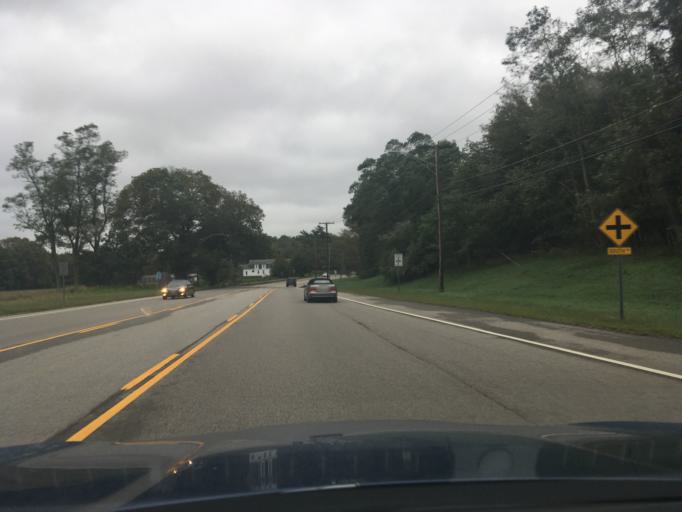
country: US
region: Rhode Island
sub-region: Washington County
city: Exeter
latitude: 41.6104
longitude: -71.4925
